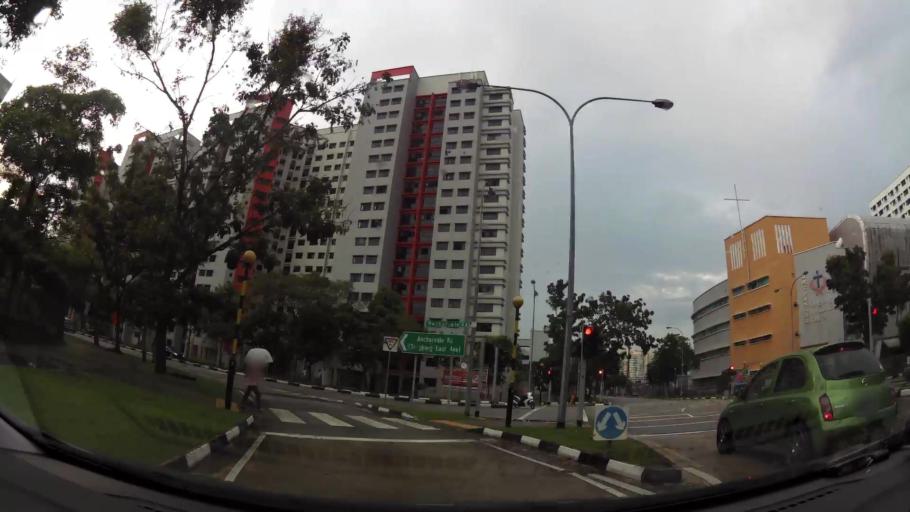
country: MY
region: Johor
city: Kampung Pasir Gudang Baru
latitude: 1.3915
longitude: 103.8867
